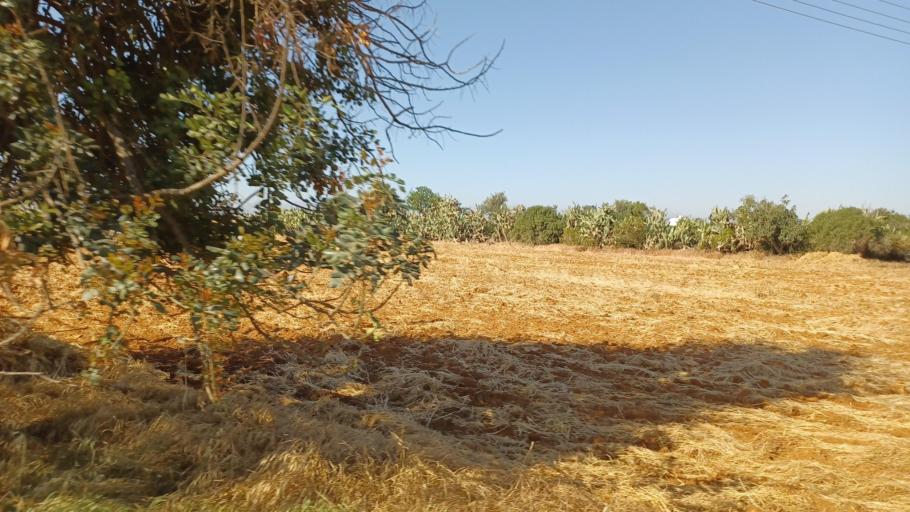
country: CY
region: Lefkosia
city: Kokkinotrimithia
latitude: 35.1445
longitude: 33.2125
